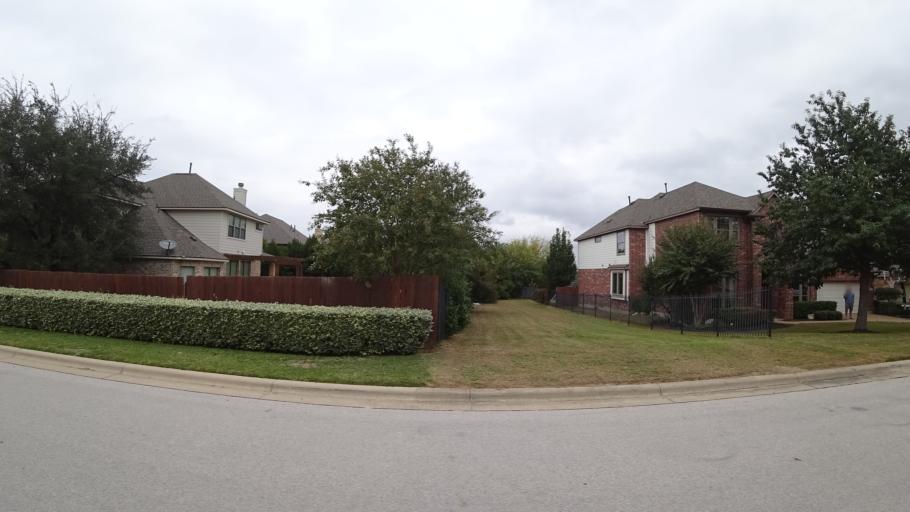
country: US
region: Texas
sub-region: Travis County
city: Hudson Bend
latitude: 30.3594
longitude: -97.9065
